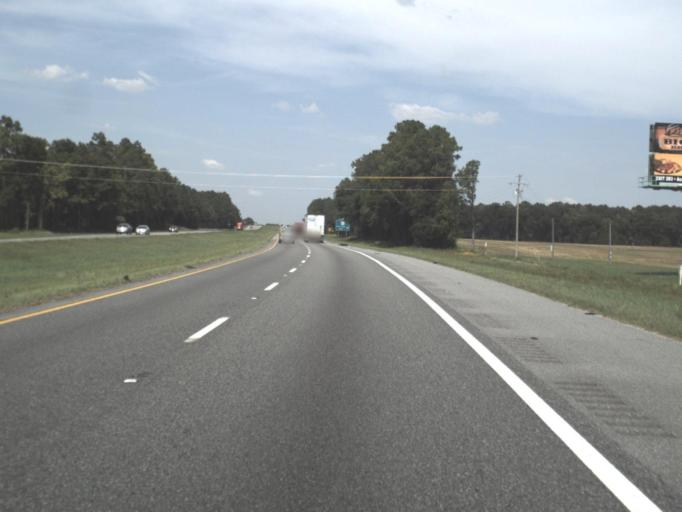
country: US
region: Florida
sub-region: Suwannee County
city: Live Oak
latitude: 30.3382
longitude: -83.0997
